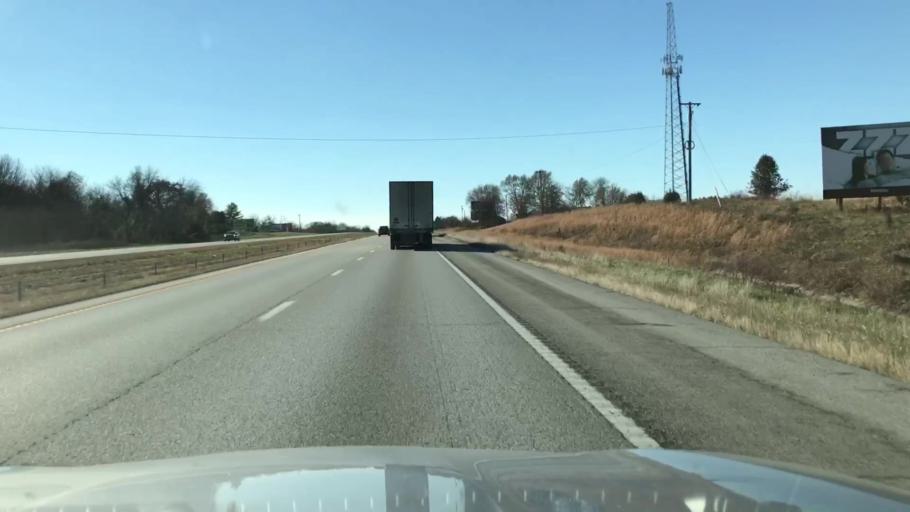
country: US
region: Missouri
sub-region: Jasper County
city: Duenweg
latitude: 37.0767
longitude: -94.3825
